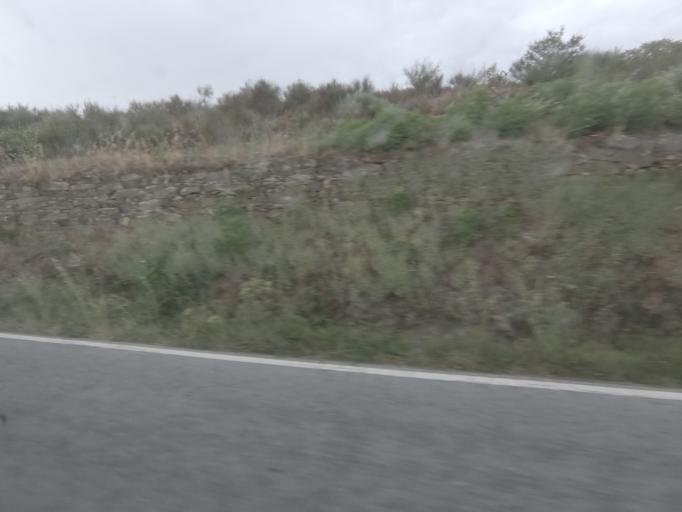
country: PT
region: Vila Real
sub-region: Peso da Regua
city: Peso da Regua
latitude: 41.1345
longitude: -7.7682
